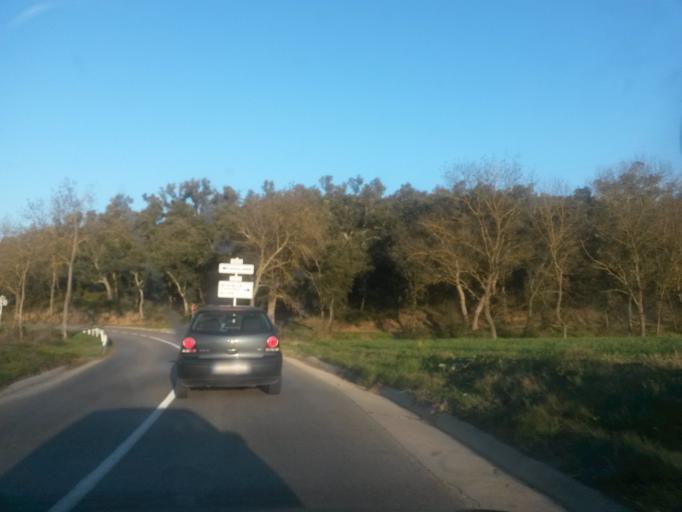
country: ES
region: Catalonia
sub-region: Provincia de Girona
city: Darnius
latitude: 42.3629
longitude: 2.8530
